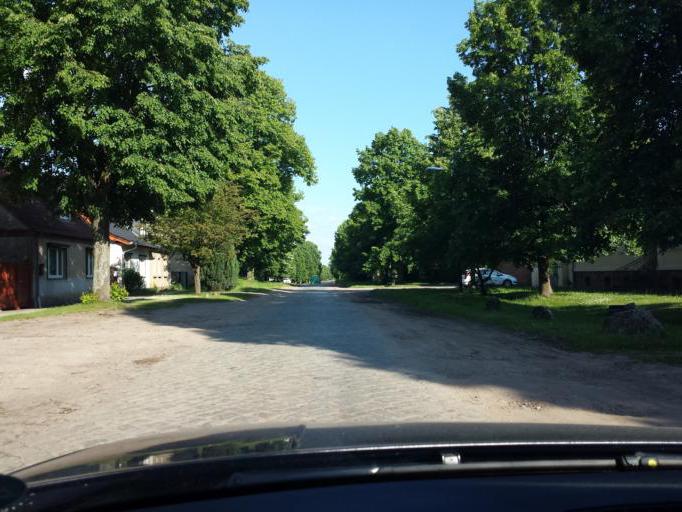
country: DE
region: Brandenburg
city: Ruthnick
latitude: 52.8814
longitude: 12.9129
